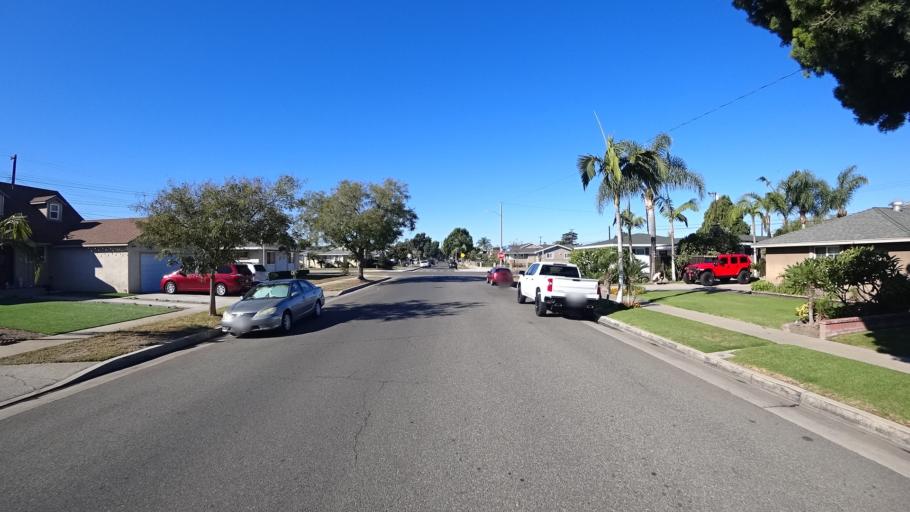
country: US
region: California
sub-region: Orange County
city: Buena Park
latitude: 33.8519
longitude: -117.9913
